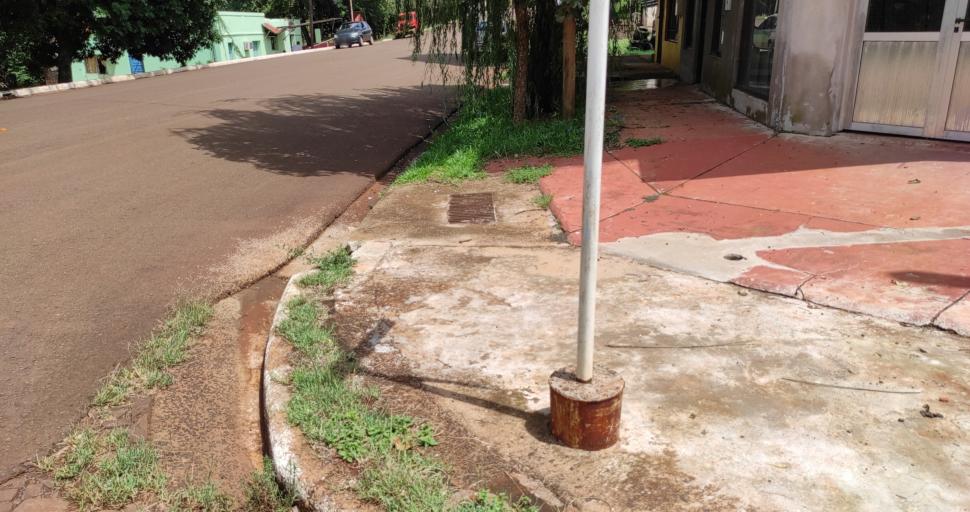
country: AR
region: Misiones
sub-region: Departamento de Apostoles
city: San Jose
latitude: -27.7708
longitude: -55.7741
